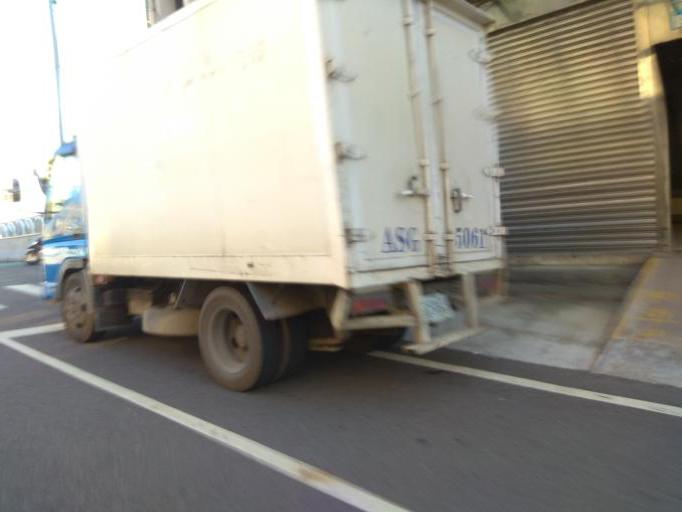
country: TW
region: Taiwan
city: Taoyuan City
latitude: 25.0650
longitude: 121.1954
